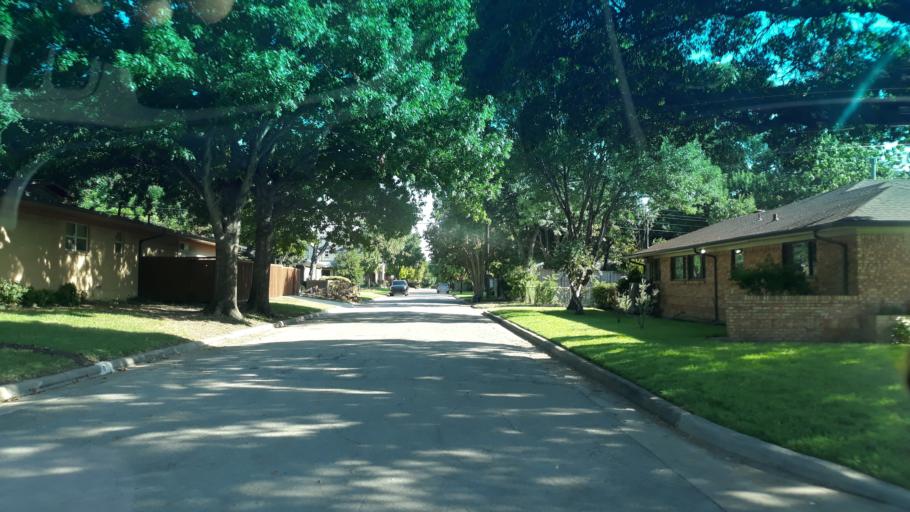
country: US
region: Texas
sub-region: Dallas County
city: Highland Park
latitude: 32.8266
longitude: -96.7581
